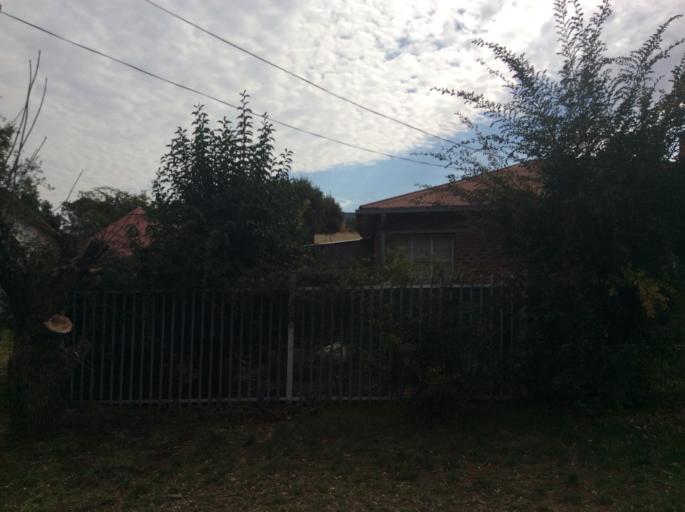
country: LS
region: Mafeteng
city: Mafeteng
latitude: -29.7311
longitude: 27.0293
